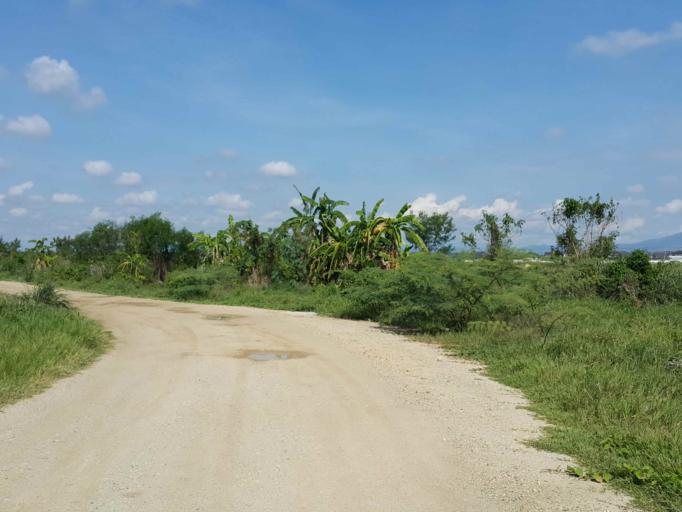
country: TH
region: Chiang Mai
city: San Kamphaeng
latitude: 18.7319
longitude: 99.0905
